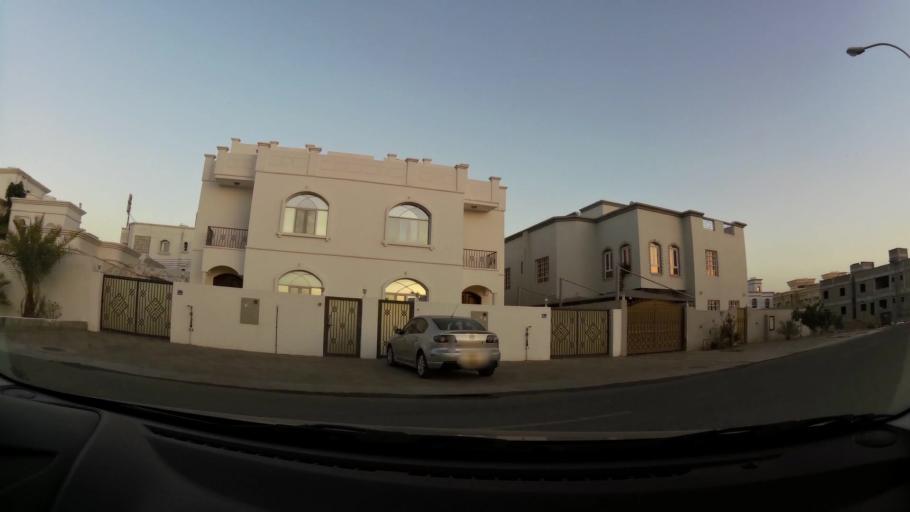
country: OM
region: Muhafazat Masqat
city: As Sib al Jadidah
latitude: 23.5920
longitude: 58.2280
